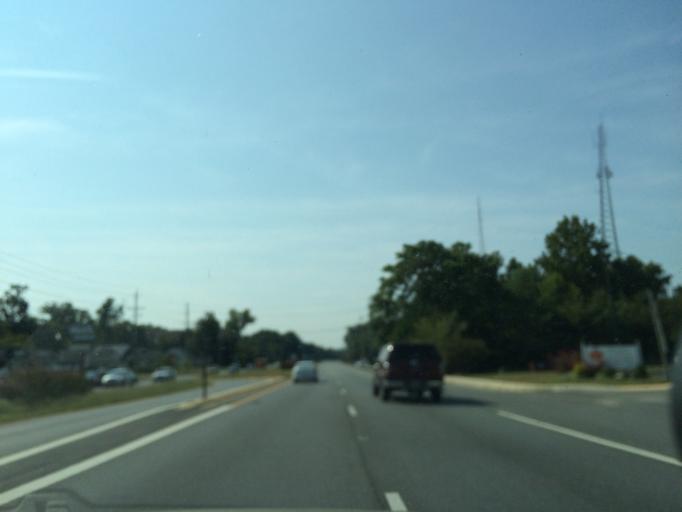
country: US
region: Maryland
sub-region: Charles County
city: La Plata
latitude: 38.5275
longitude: -76.9827
